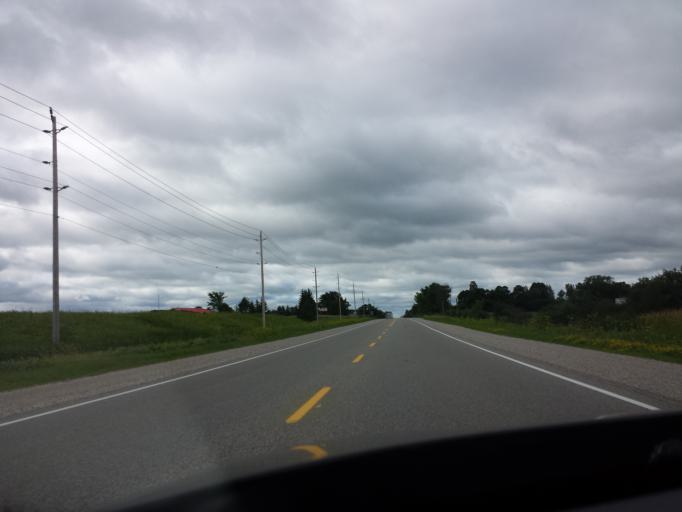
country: CA
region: Ontario
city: Perth
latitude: 44.9562
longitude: -76.2339
